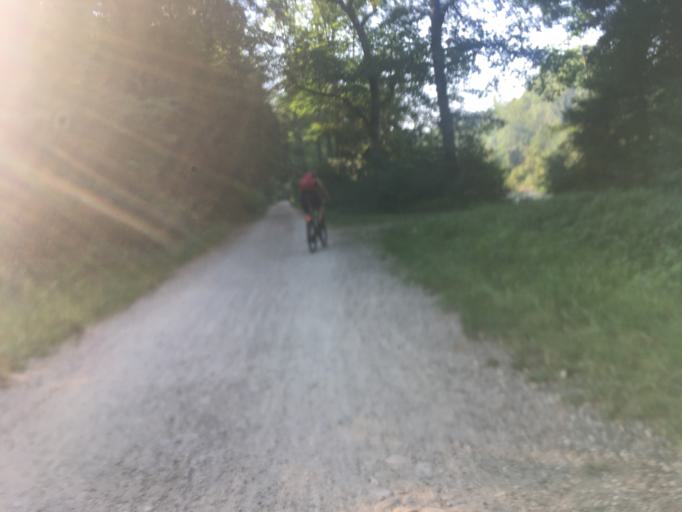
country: CH
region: Bern
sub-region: Emmental District
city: Oberburg
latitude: 47.0281
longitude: 7.6444
